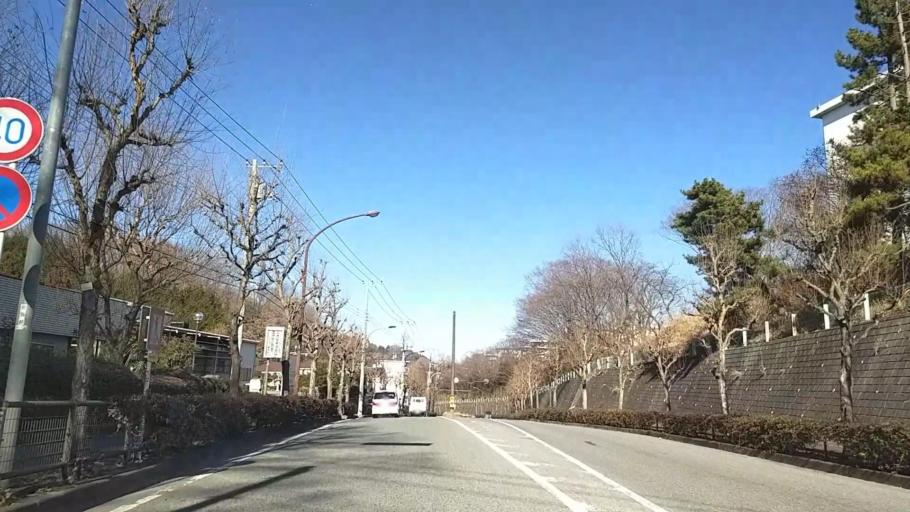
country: JP
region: Tokyo
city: Hachioji
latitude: 35.6223
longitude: 139.2871
